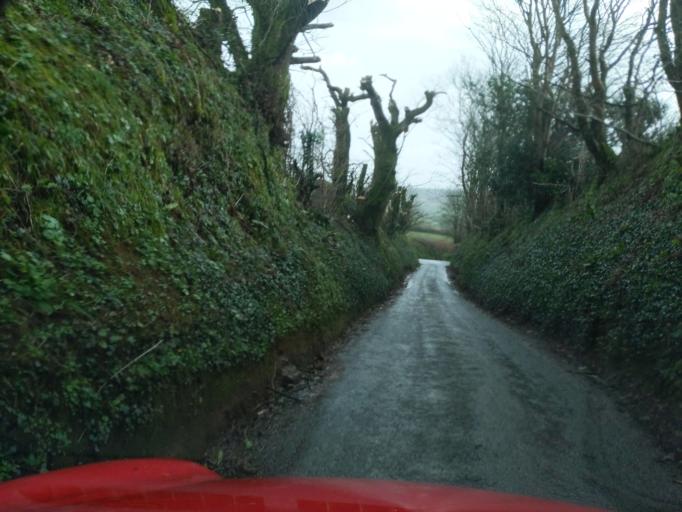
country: GB
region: England
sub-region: Devon
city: Ivybridge
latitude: 50.3633
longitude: -3.9303
